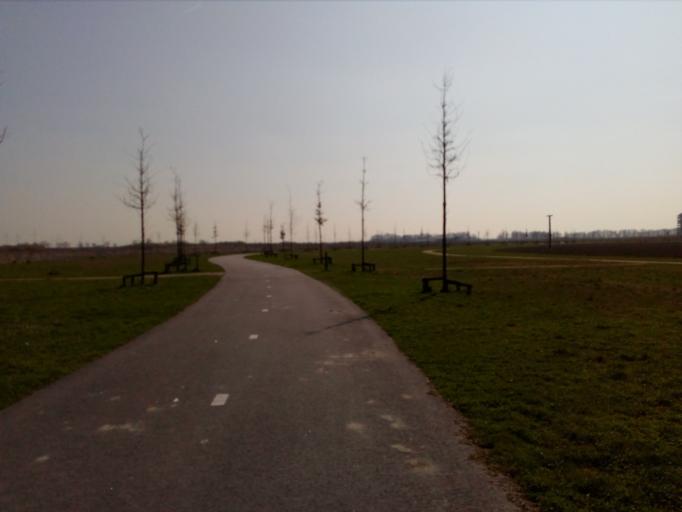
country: NL
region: South Holland
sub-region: Gemeente Rijnwoude
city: Benthuizen
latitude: 52.0713
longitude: 4.5458
